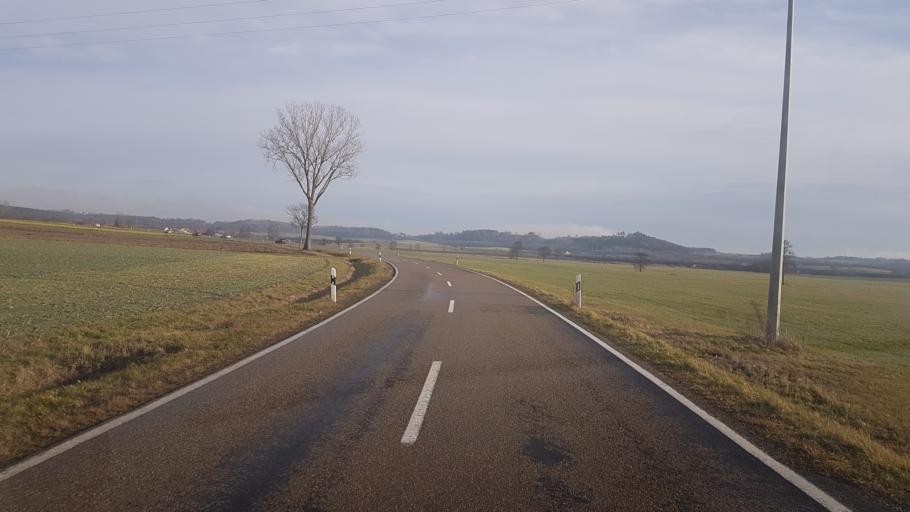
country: DE
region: Bavaria
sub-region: Regierungsbezirk Mittelfranken
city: Schnelldorf
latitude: 49.2234
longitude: 10.2304
